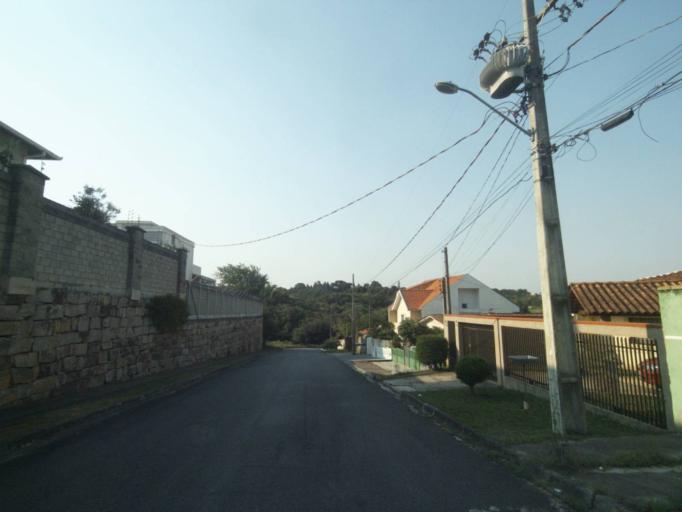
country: BR
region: Parana
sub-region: Curitiba
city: Curitiba
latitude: -25.4927
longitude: -49.2668
